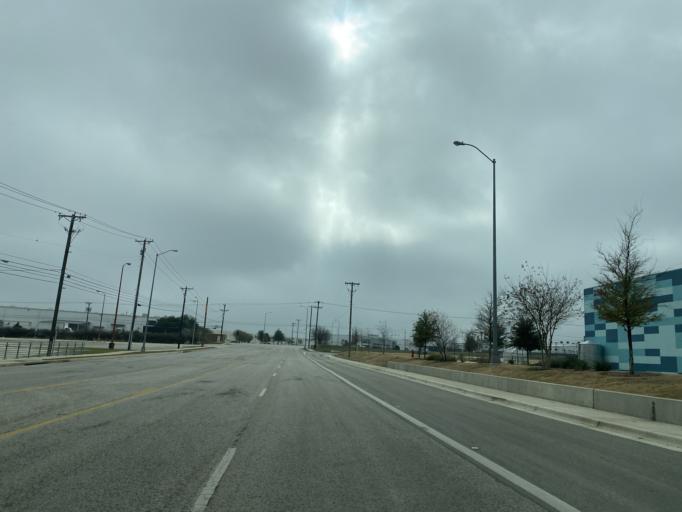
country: US
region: Texas
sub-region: Williamson County
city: Round Rock
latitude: 30.5385
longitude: -97.6888
